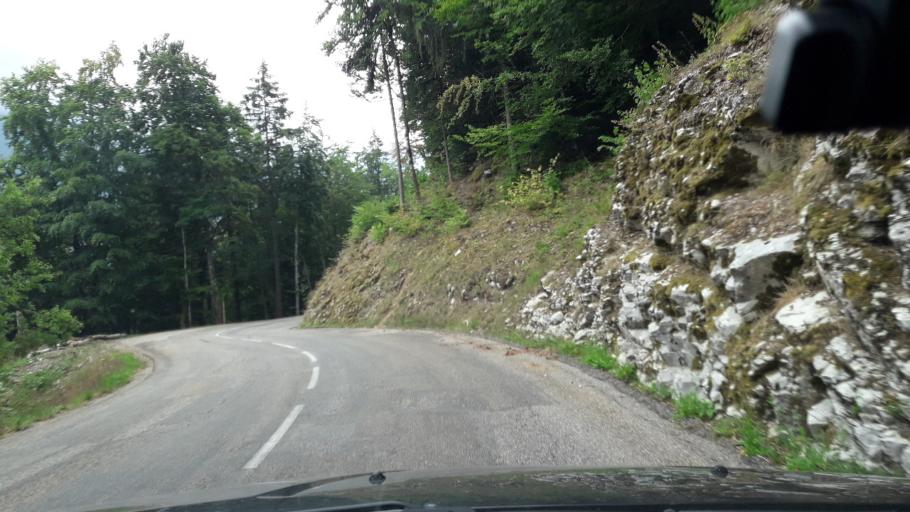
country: FR
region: Rhone-Alpes
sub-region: Departement de la Savoie
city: Vimines
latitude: 45.4521
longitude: 5.8701
